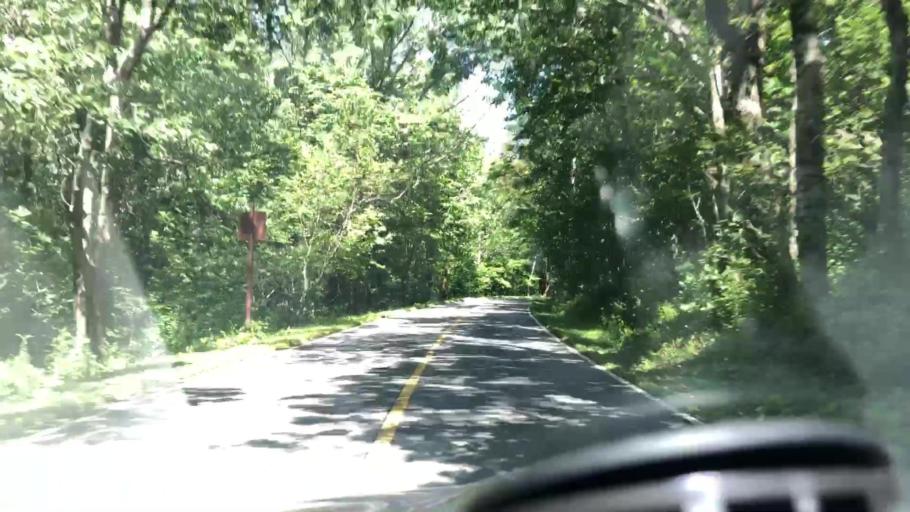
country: US
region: Massachusetts
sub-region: Berkshire County
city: Adams
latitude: 42.6021
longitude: -73.2008
